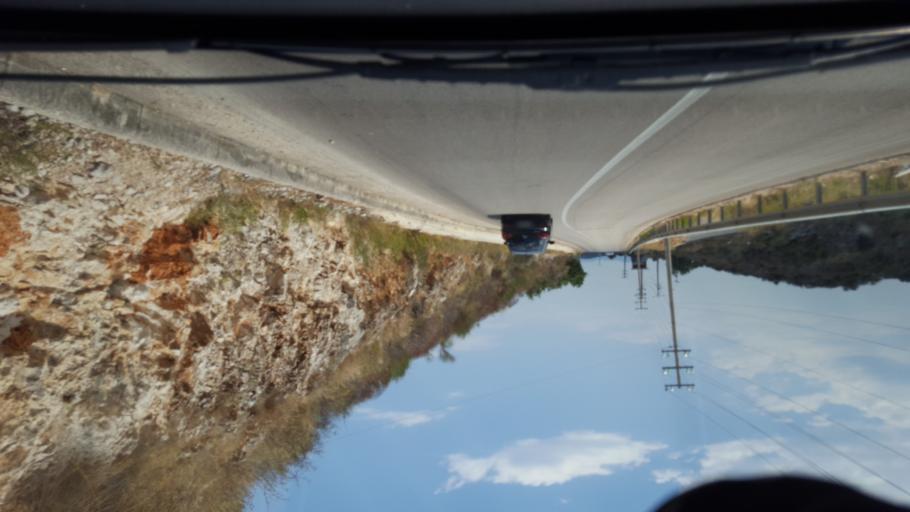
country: AL
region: Vlore
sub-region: Rrethi i Sarandes
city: Xarre
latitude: 39.7926
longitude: 20.0094
